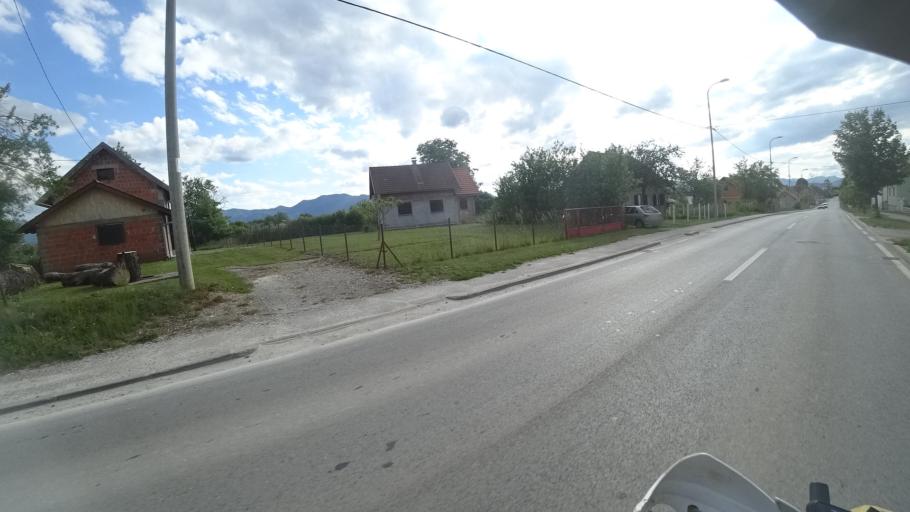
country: HR
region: Licko-Senjska
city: Gospic
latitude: 44.5368
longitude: 15.3905
